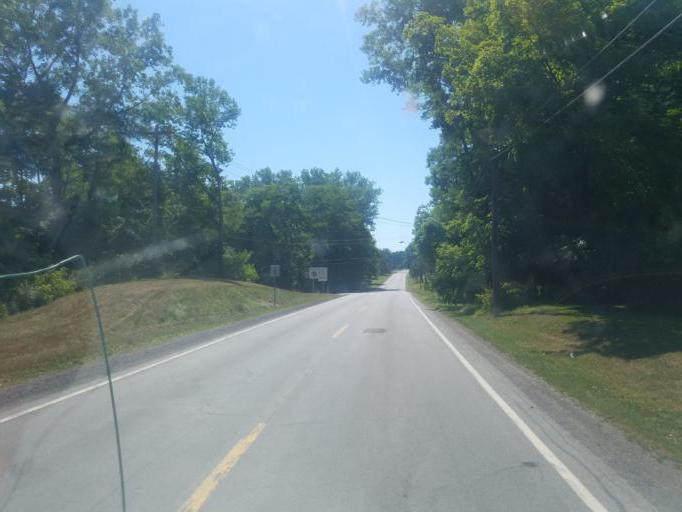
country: US
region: New York
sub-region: Ontario County
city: Phelps
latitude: 42.9325
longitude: -77.0073
